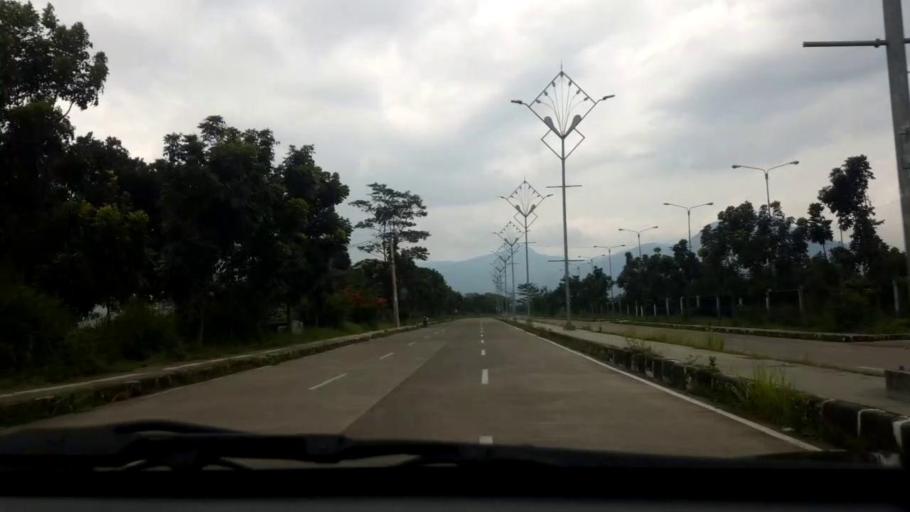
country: ID
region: West Java
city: Cileunyi
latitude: -6.9562
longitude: 107.7106
